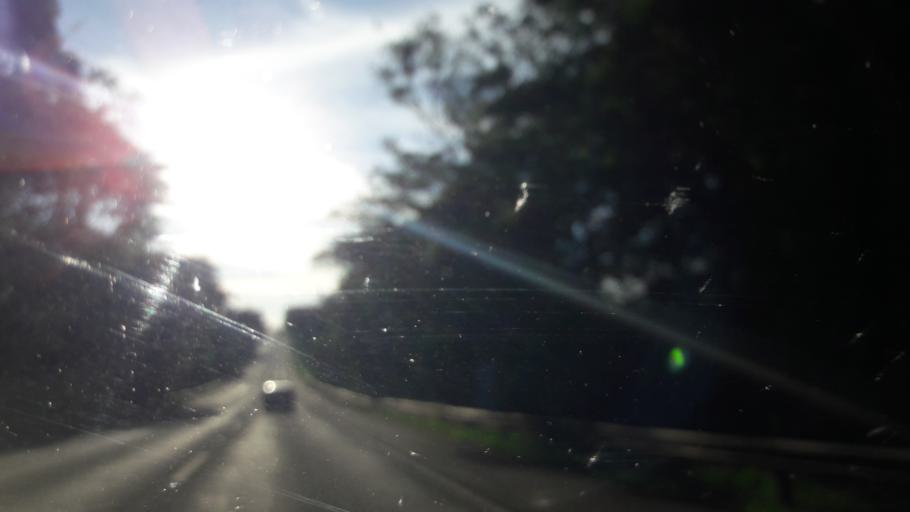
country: BR
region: Parana
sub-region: Moreira Sales
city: Moreira Sales
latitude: -24.3405
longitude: -52.7126
